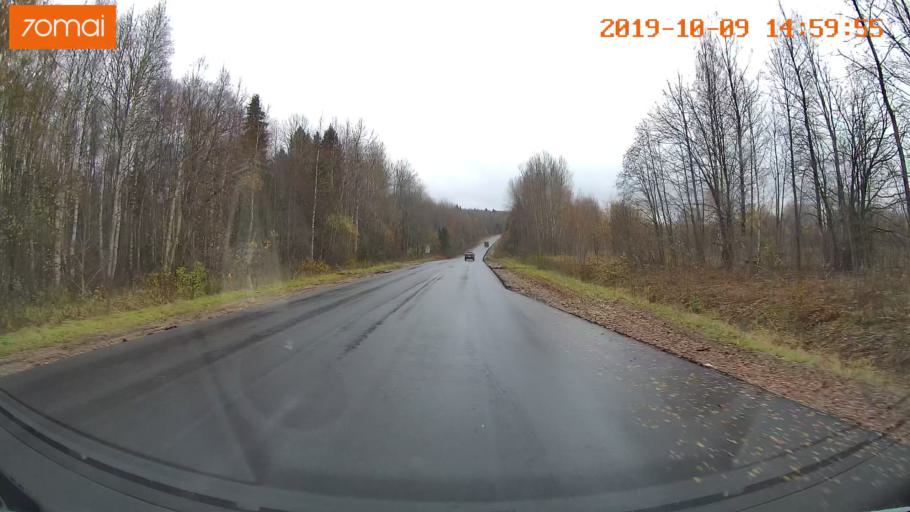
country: RU
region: Kostroma
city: Chistyye Bory
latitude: 58.3149
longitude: 41.6737
